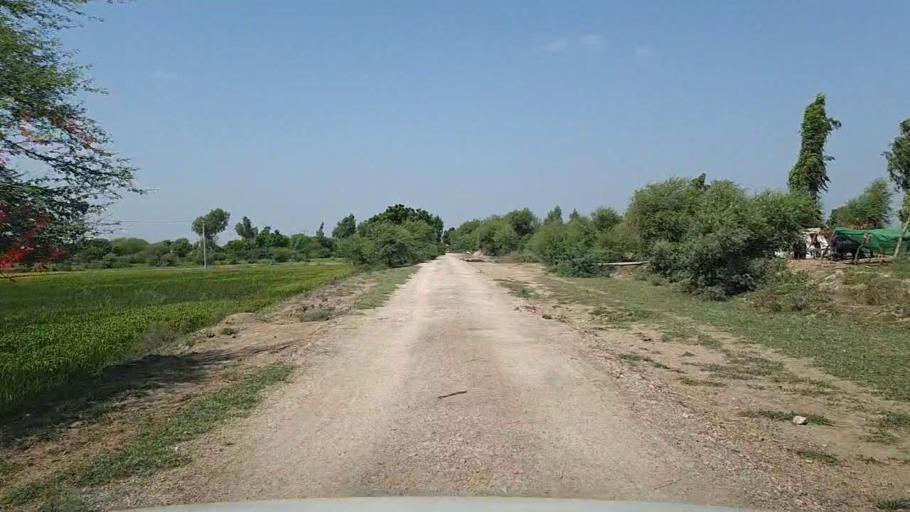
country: PK
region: Sindh
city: Kario
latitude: 24.8893
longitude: 68.6781
